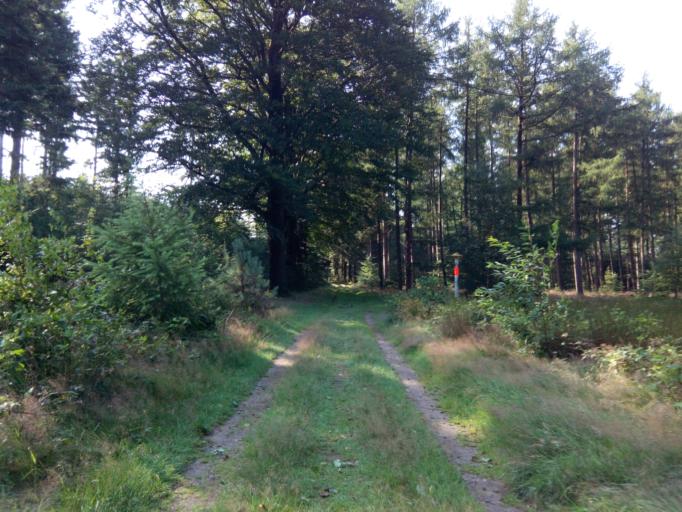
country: NL
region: Utrecht
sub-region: Gemeente Utrechtse Heuvelrug
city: Maarn
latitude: 52.0775
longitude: 5.3470
